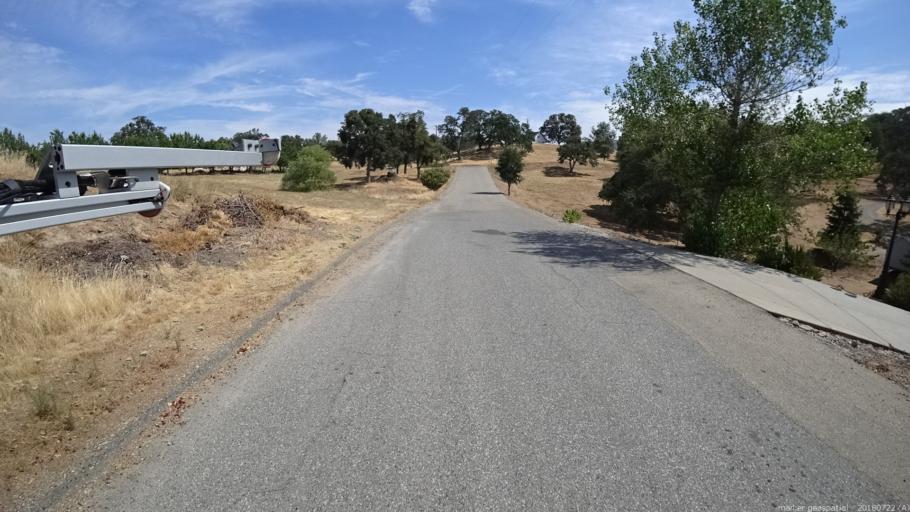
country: US
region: California
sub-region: Madera County
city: Coarsegold
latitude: 37.2615
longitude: -119.7134
